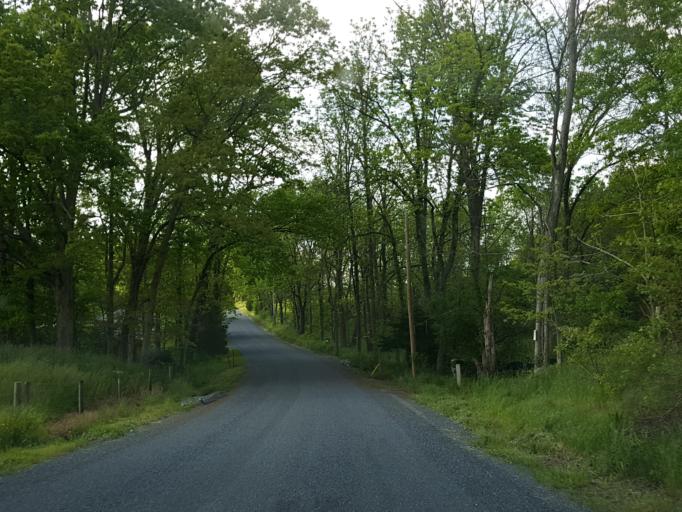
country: US
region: Pennsylvania
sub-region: Lebanon County
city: Campbelltown
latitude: 40.2173
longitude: -76.5726
